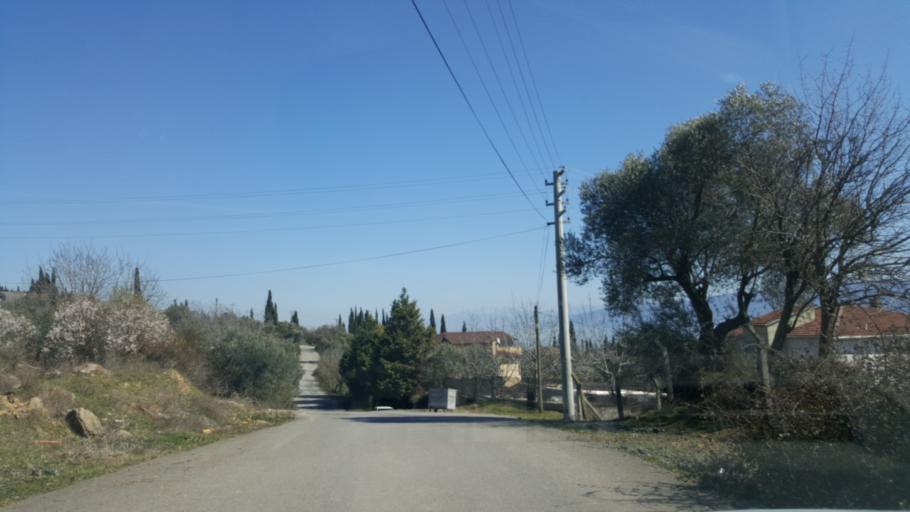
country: TR
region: Kocaeli
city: Tavsancil
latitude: 40.7770
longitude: 29.5728
